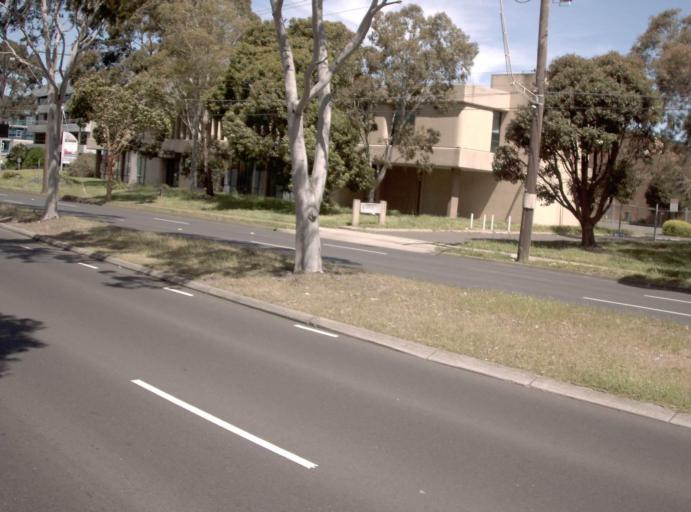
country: AU
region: Victoria
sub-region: Monash
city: Notting Hill
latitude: -37.8981
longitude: 145.1436
